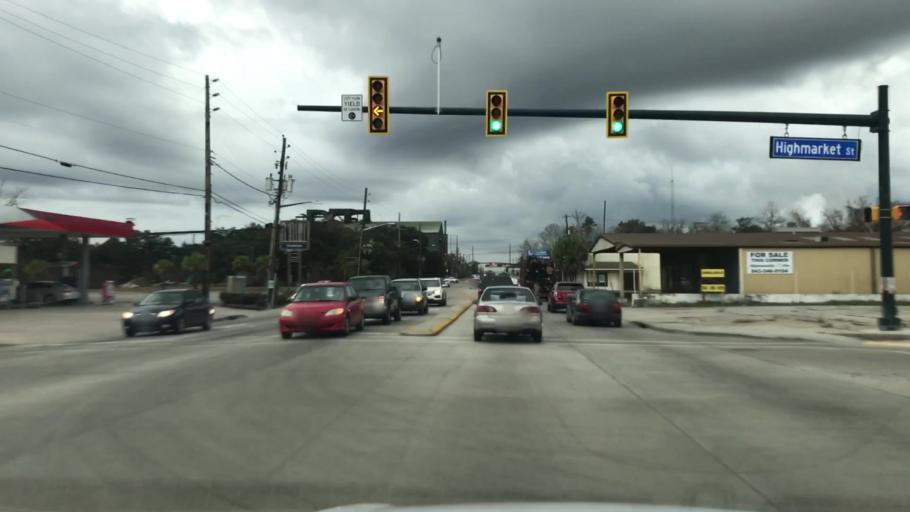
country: US
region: South Carolina
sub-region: Georgetown County
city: Georgetown
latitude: 33.3737
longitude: -79.2887
